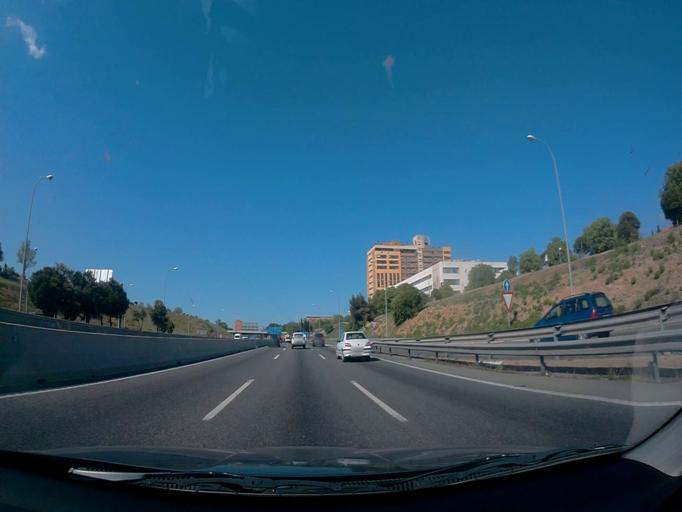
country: ES
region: Madrid
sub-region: Provincia de Madrid
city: Vicalvaro
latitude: 40.3956
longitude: -3.6280
